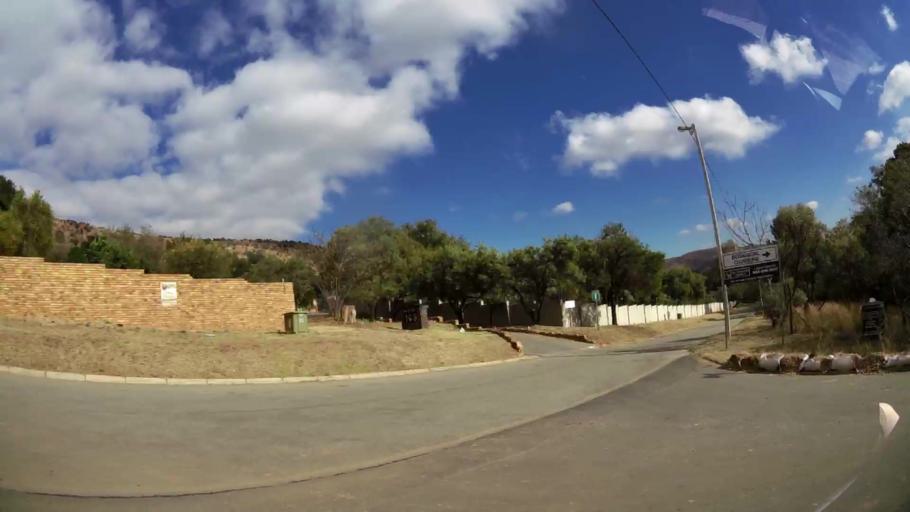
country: ZA
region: Gauteng
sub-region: West Rand District Municipality
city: Muldersdriseloop
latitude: -26.0926
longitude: 27.8521
